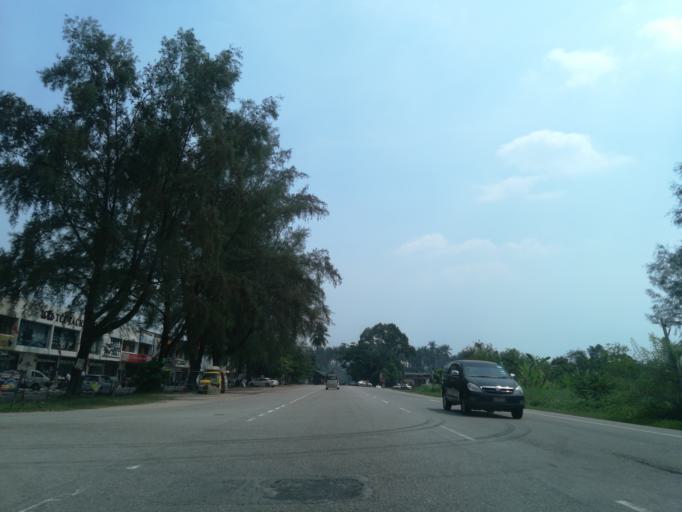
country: MY
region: Kedah
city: Kulim
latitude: 5.4250
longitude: 100.5369
